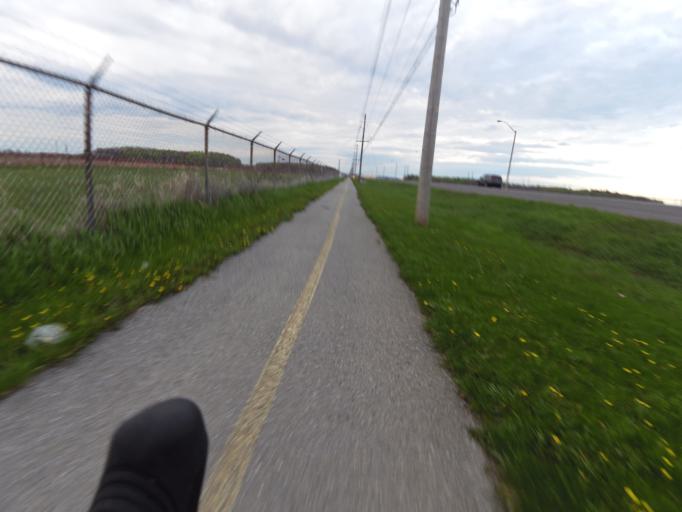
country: CA
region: Ontario
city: Bells Corners
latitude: 45.3071
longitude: -75.7684
